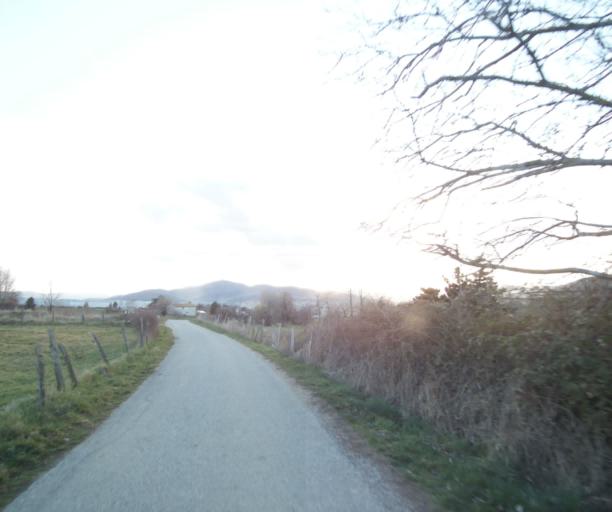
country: FR
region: Rhone-Alpes
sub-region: Departement de l'Ardeche
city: Davezieux
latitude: 45.2448
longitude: 4.6974
